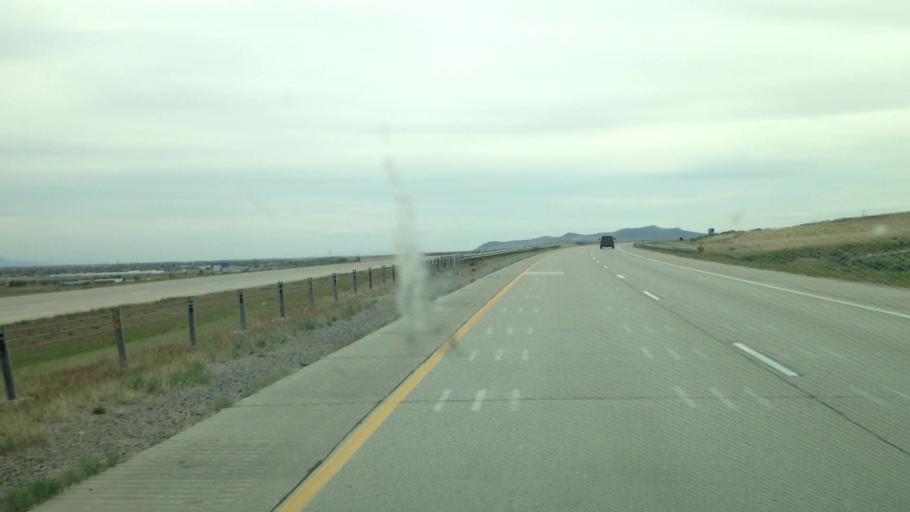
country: US
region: Utah
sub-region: Box Elder County
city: Garland
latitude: 41.7572
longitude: -112.1817
